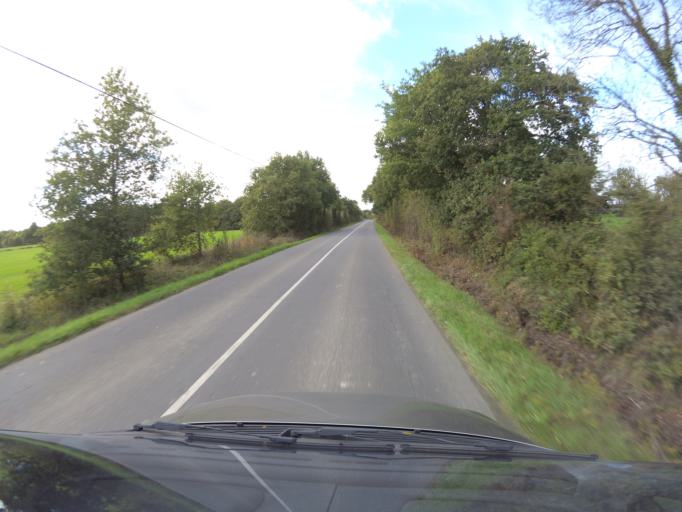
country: FR
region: Pays de la Loire
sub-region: Departement de la Loire-Atlantique
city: Heric
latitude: 47.4098
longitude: -1.6296
